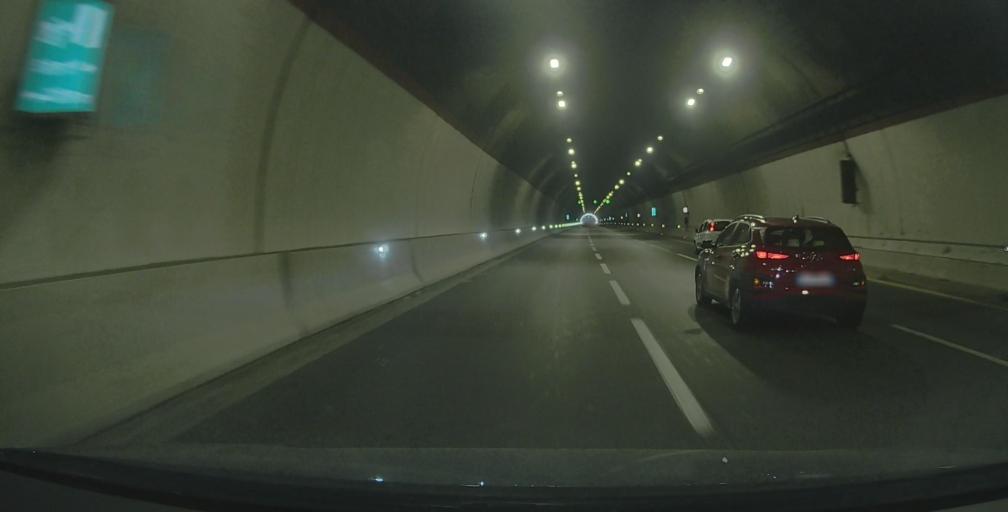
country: IT
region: Campania
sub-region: Provincia di Salerno
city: Fuorni
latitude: 40.6646
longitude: 14.8587
